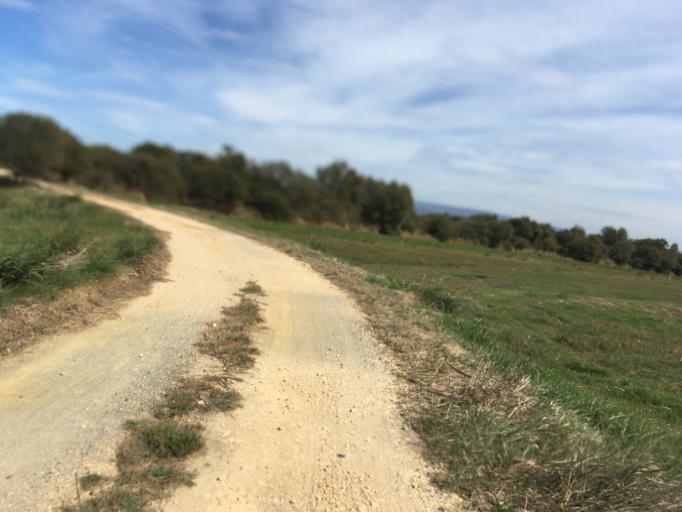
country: PT
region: Aveiro
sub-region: Estarreja
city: Estarreja
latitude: 40.7291
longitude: -8.5986
